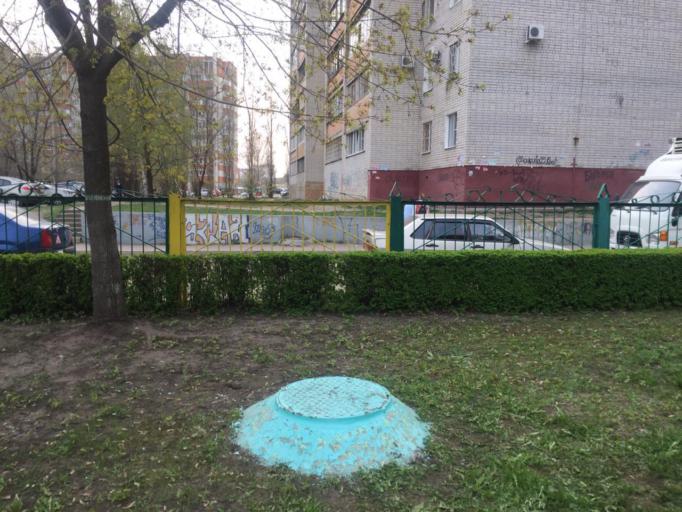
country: RU
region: Voronezj
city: Podgornoye
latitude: 51.6896
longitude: 39.1327
